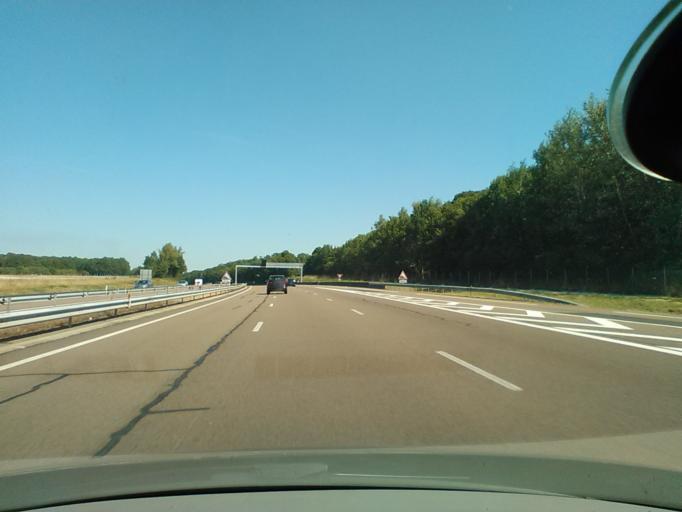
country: FR
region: Bourgogne
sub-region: Departement de l'Yonne
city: Aillant-sur-Tholon
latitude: 47.9112
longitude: 3.2975
